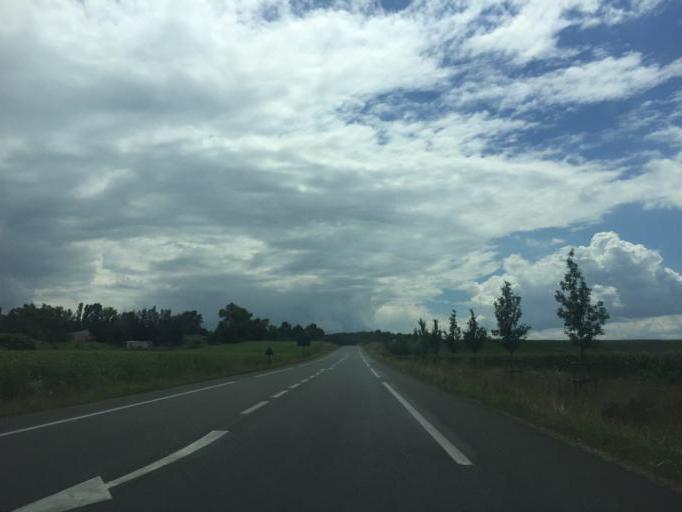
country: FR
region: Rhone-Alpes
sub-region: Departement de l'Isere
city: Chavanoz
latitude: 45.7896
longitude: 5.1320
